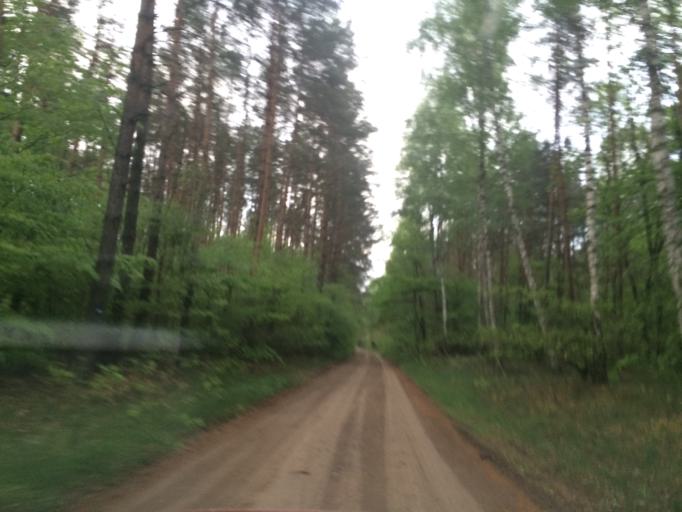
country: PL
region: Warmian-Masurian Voivodeship
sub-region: Powiat nowomiejski
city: Kurzetnik
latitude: 53.3557
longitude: 19.5177
